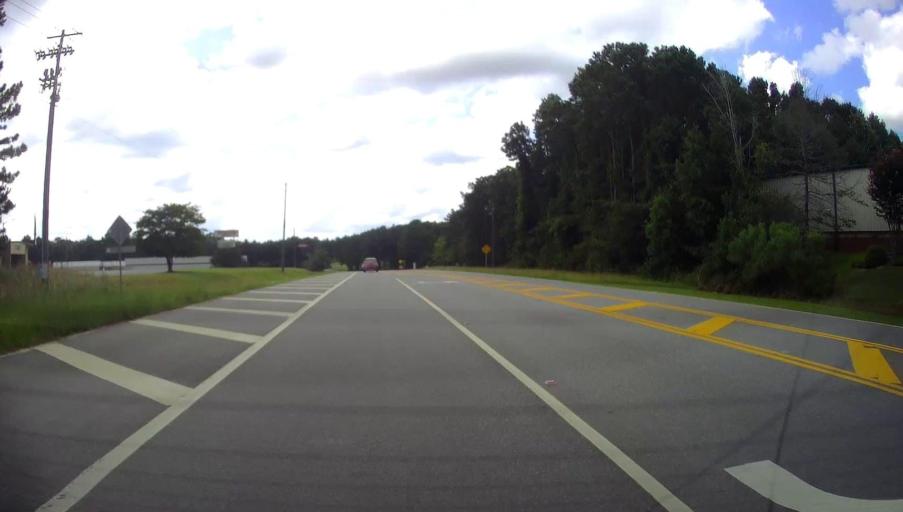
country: US
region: Alabama
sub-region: Russell County
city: Phenix City
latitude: 32.5636
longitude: -84.9396
